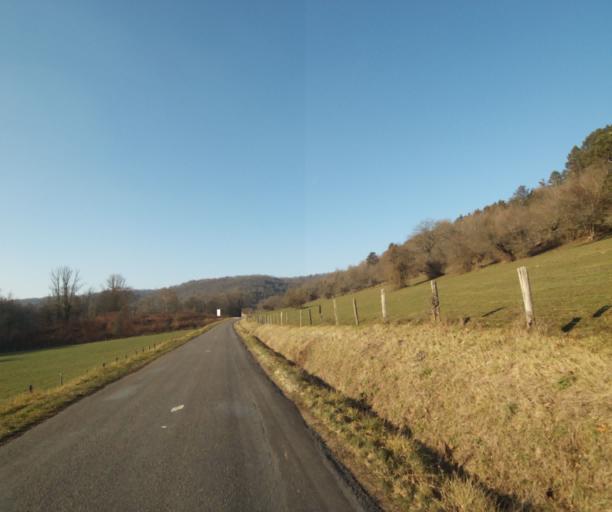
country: FR
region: Champagne-Ardenne
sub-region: Departement de la Haute-Marne
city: Chevillon
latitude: 48.5018
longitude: 5.1796
